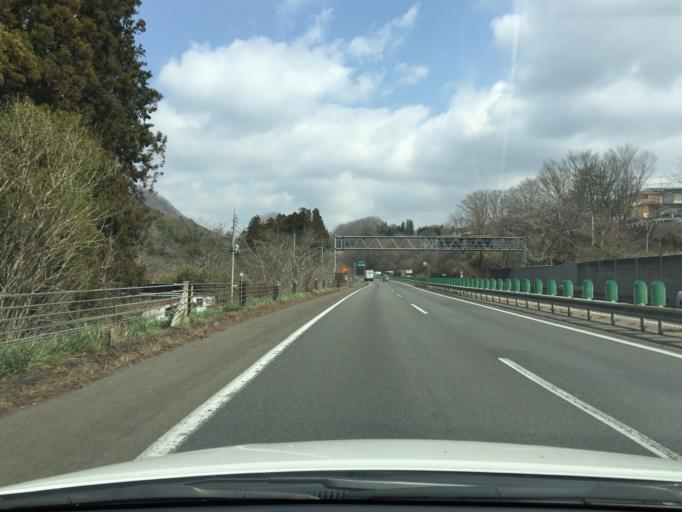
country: JP
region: Miyagi
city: Sendai
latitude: 38.2210
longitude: 140.8018
